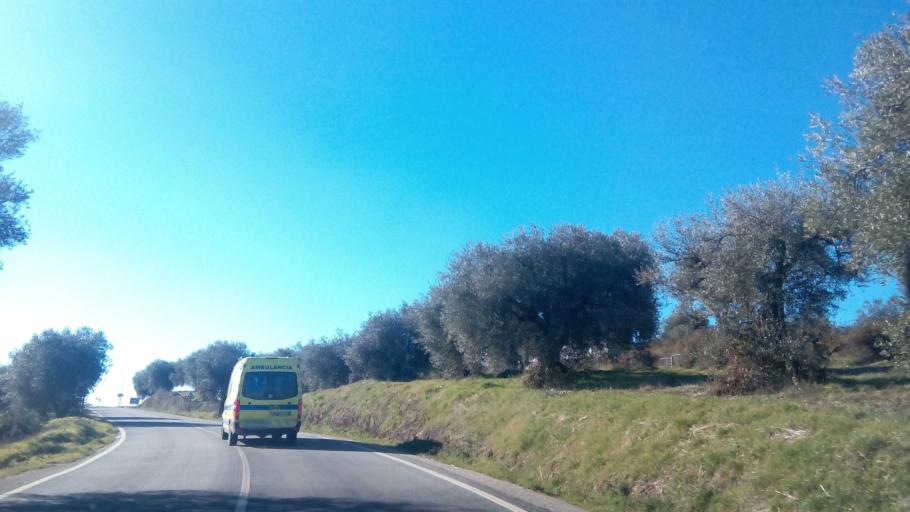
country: PT
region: Braganca
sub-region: Vimioso
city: Vimioso
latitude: 41.5972
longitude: -6.5800
